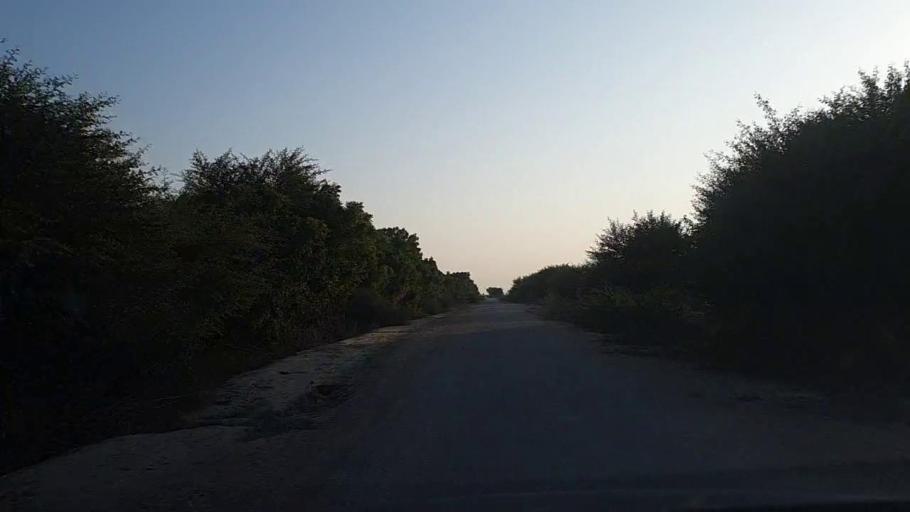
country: PK
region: Sindh
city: Naukot
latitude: 24.8409
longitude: 69.3117
